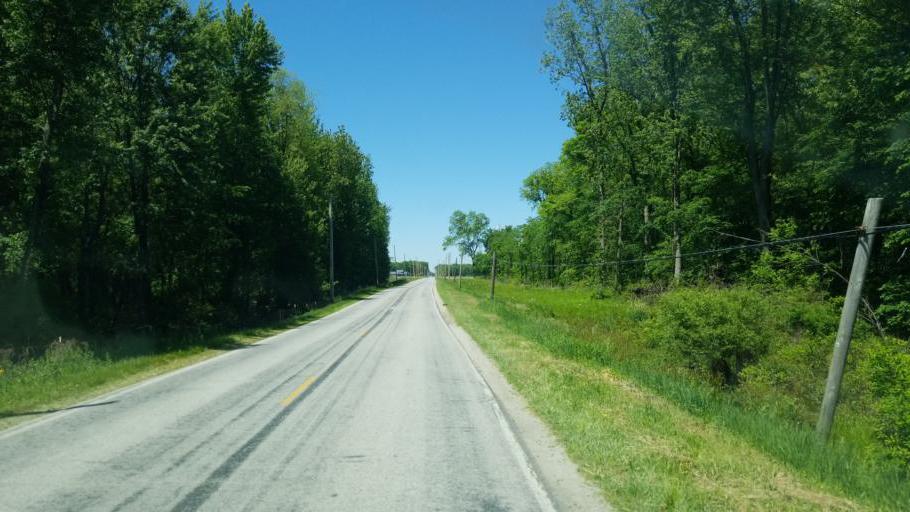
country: US
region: Ohio
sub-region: Shelby County
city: Fort Loramie
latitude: 40.3548
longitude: -84.3297
